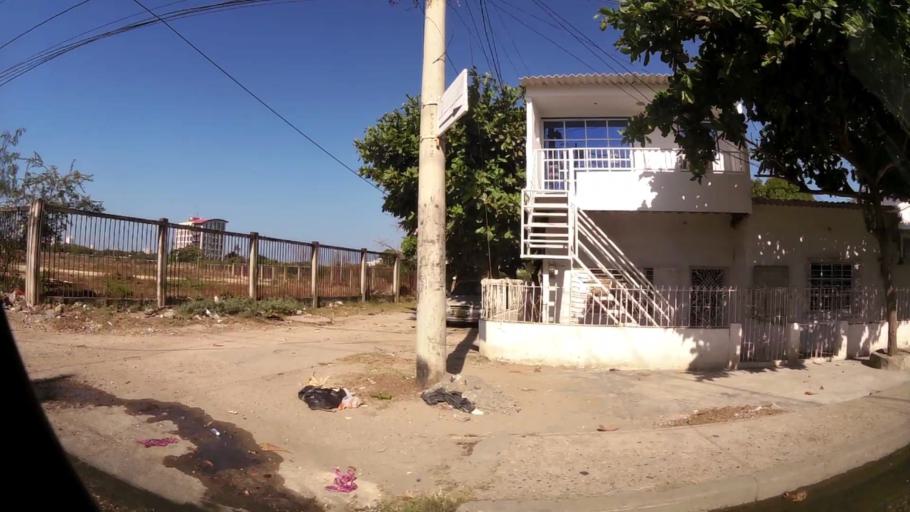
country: CO
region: Bolivar
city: Cartagena
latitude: 10.4298
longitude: -75.5374
